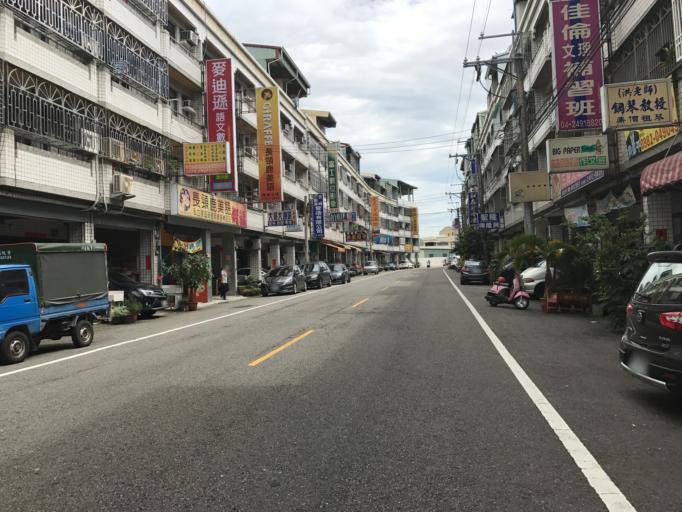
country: TW
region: Taiwan
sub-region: Taichung City
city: Taichung
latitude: 24.0846
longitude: 120.7016
